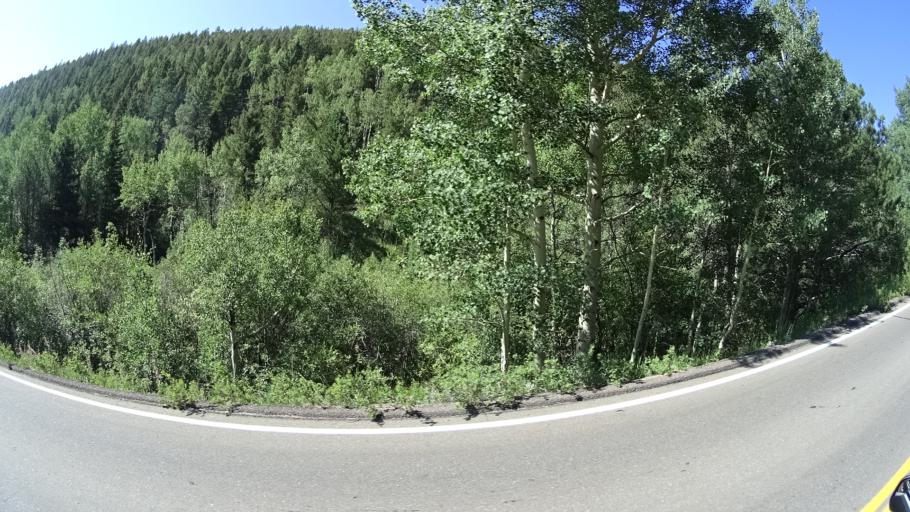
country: US
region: Colorado
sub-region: El Paso County
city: Cascade-Chipita Park
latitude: 38.9032
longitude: -105.0083
